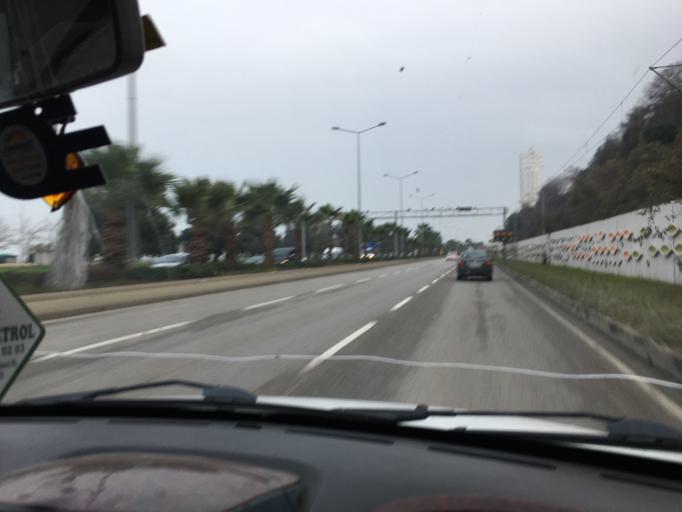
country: TR
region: Samsun
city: Samsun
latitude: 41.3179
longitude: 36.3314
